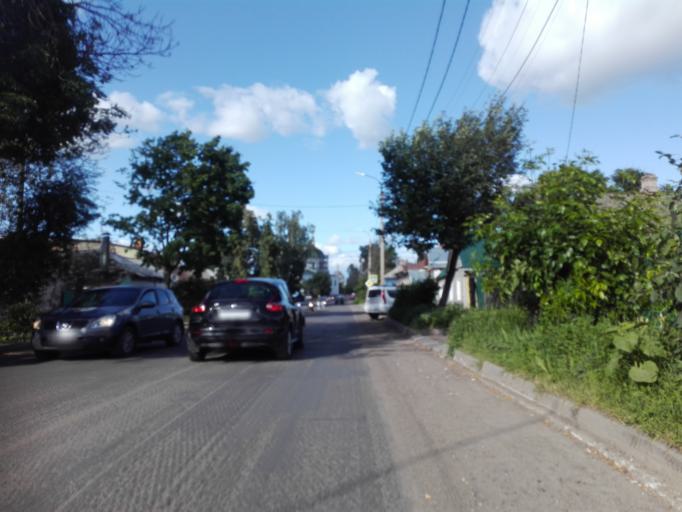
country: RU
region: Orjol
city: Orel
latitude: 52.9581
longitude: 36.0563
